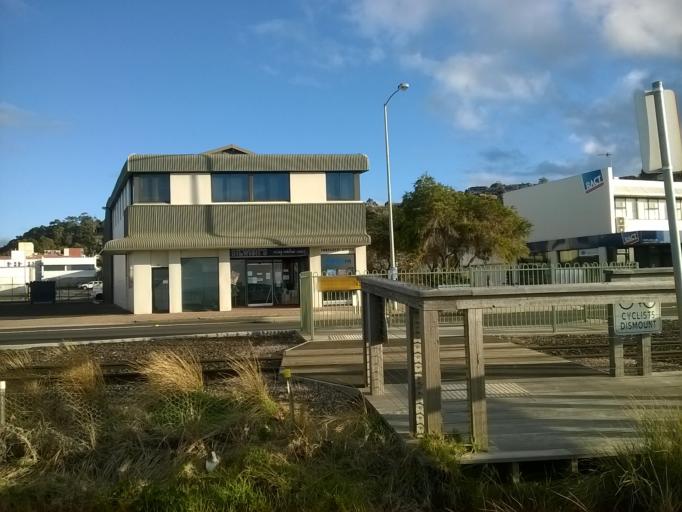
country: AU
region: Tasmania
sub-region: Burnie
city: Burnie
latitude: -41.0486
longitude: 145.9037
